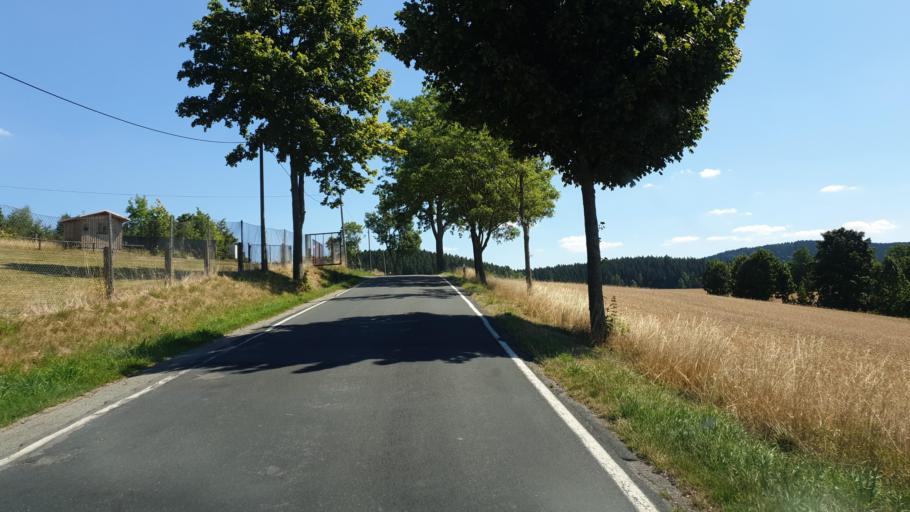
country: DE
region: Saxony
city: Sosa
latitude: 50.5013
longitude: 12.6588
